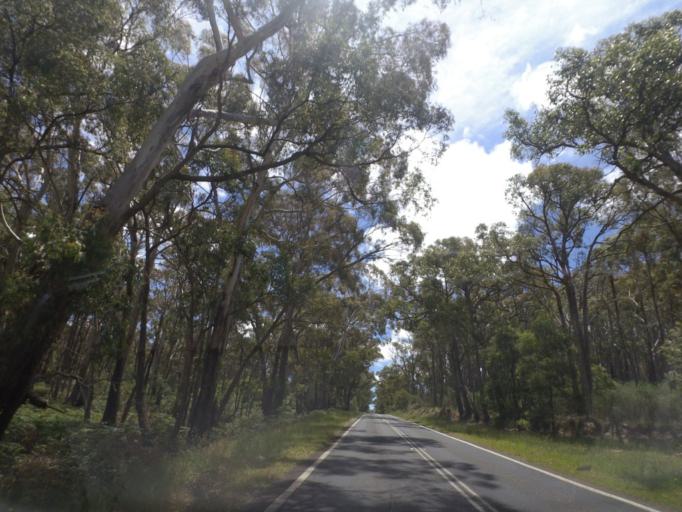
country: AU
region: Victoria
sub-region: Mount Alexander
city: Castlemaine
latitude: -37.3118
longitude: 144.1660
